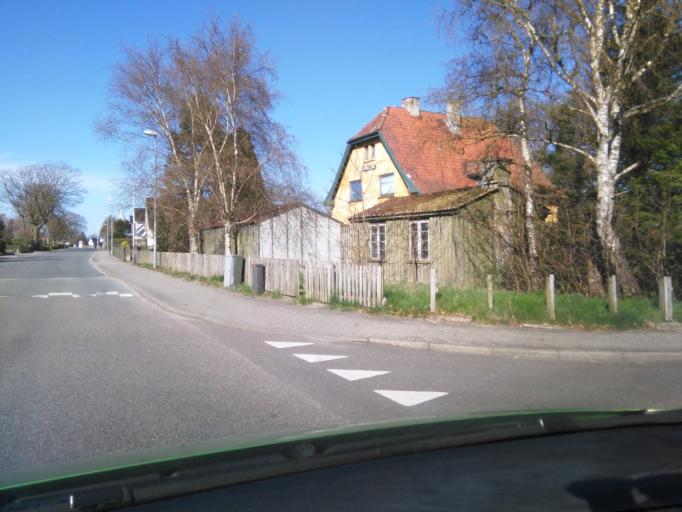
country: DK
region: South Denmark
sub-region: Varde Kommune
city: Oksbol
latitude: 55.6288
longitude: 8.2790
